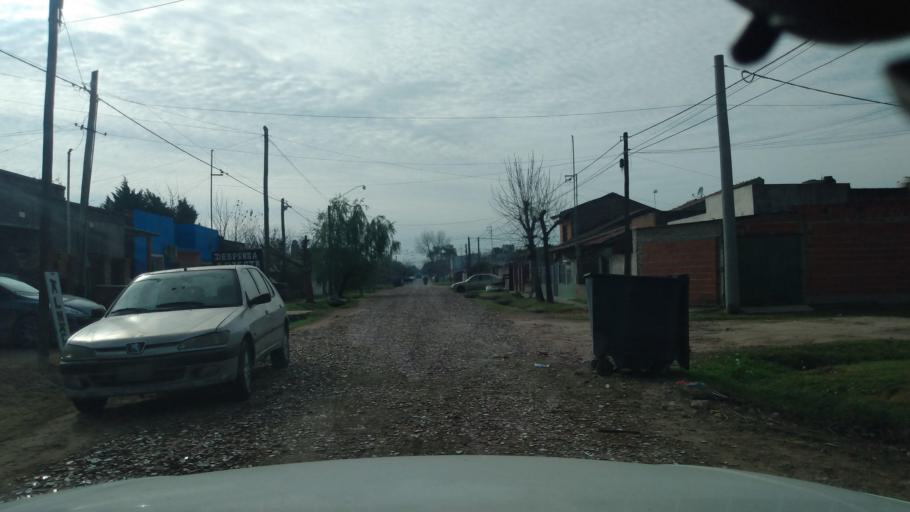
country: AR
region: Buenos Aires
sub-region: Partido de Lujan
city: Lujan
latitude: -34.5792
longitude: -59.1272
